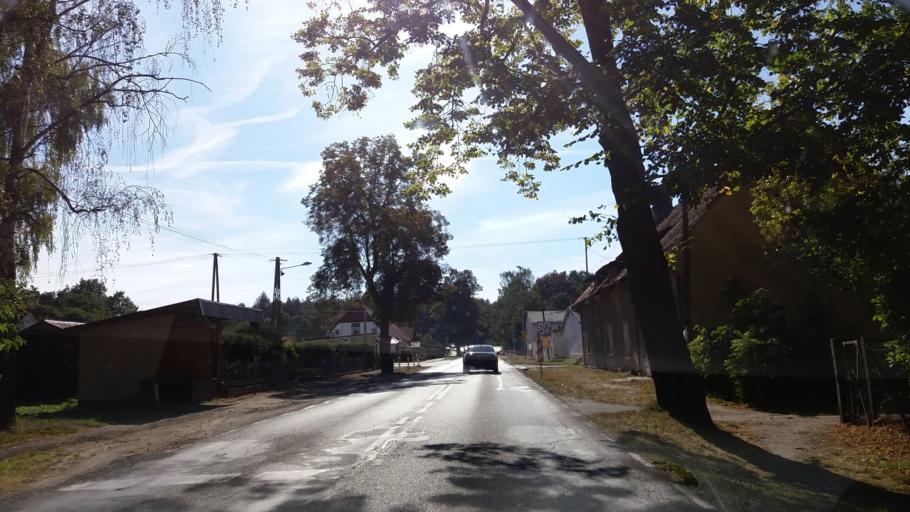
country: PL
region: Greater Poland Voivodeship
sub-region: Powiat miedzychodzki
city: Miedzychod
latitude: 52.5674
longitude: 15.8941
